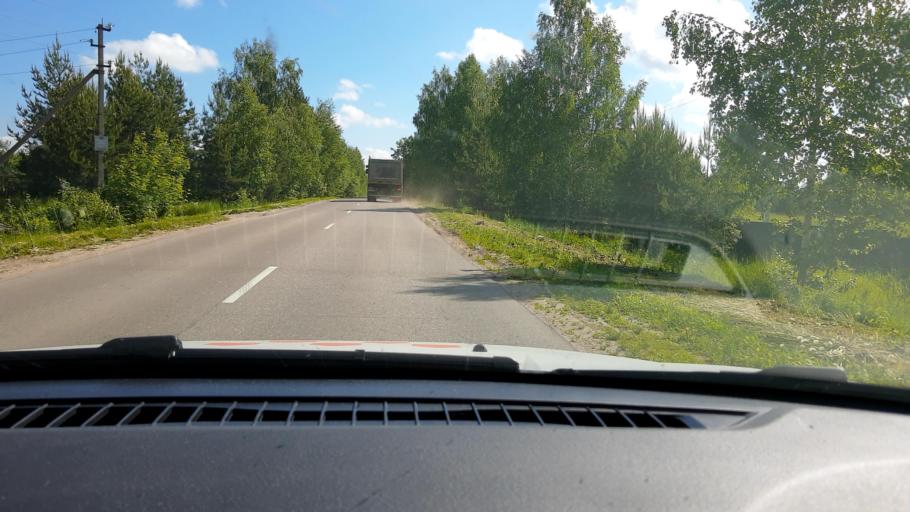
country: RU
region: Nizjnij Novgorod
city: Dal'neye Konstantinovo
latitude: 55.9283
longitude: 43.9875
